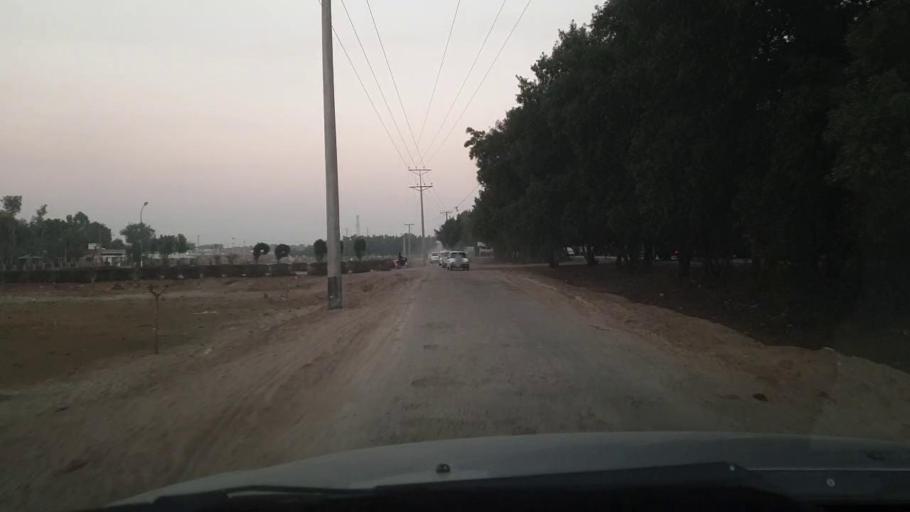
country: PK
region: Sindh
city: Mirpur Mathelo
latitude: 28.0280
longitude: 69.5792
